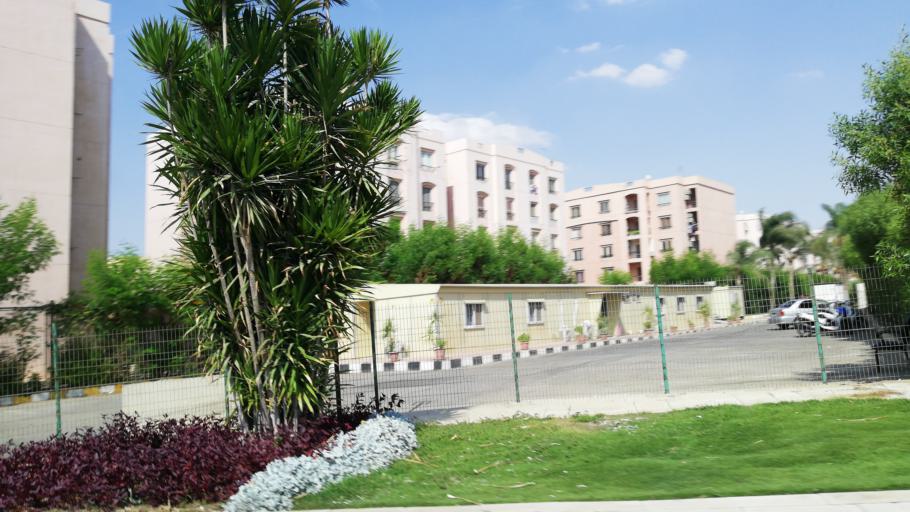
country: EG
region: Muhafazat al Qalyubiyah
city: Al Khankah
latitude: 30.0592
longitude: 31.4879
